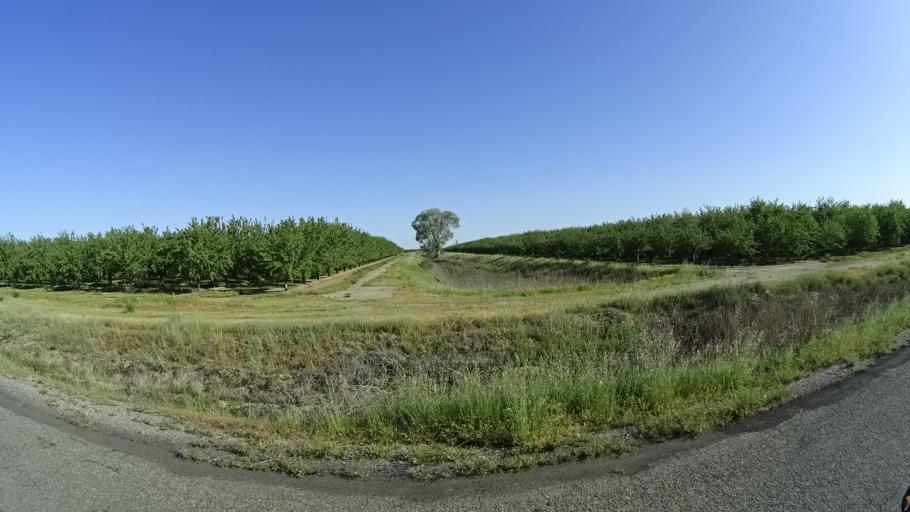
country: US
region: California
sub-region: Glenn County
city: Orland
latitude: 39.6961
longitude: -122.1175
